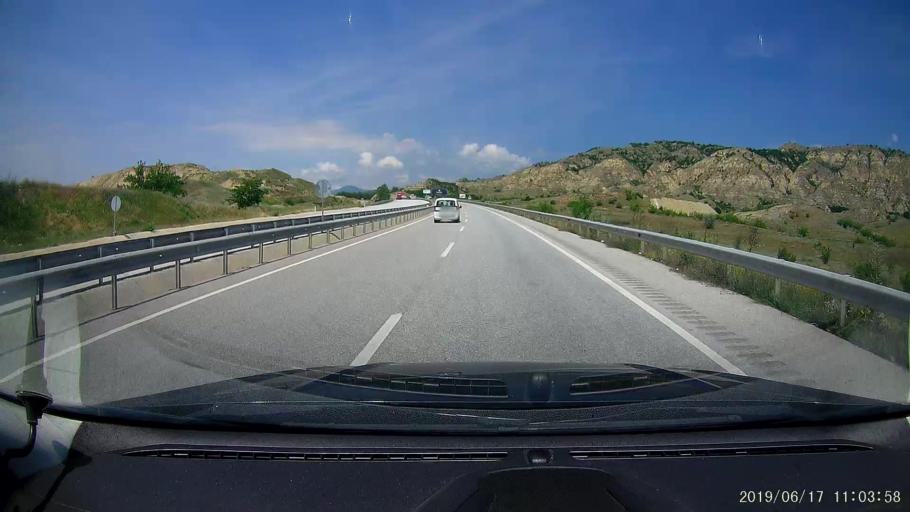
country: TR
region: Kastamonu
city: Tosya
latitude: 41.0202
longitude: 34.1050
